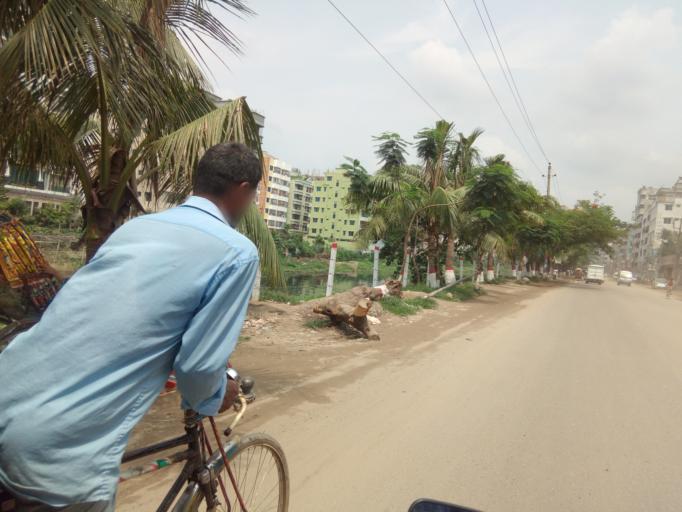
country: BD
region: Dhaka
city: Paltan
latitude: 23.7661
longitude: 90.4262
